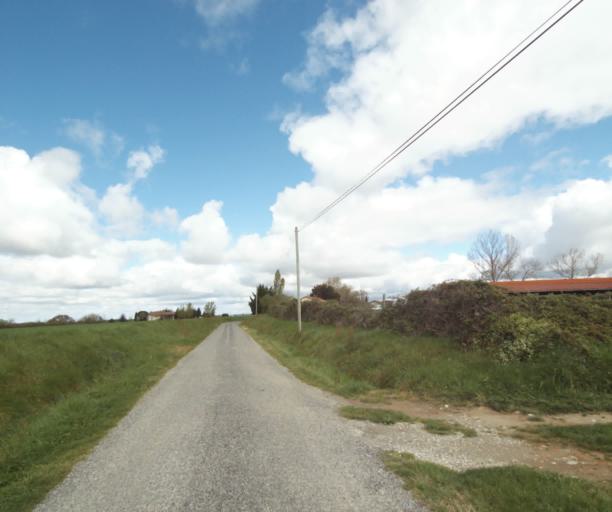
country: FR
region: Midi-Pyrenees
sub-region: Departement de l'Ariege
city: Saverdun
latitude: 43.2230
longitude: 1.5786
